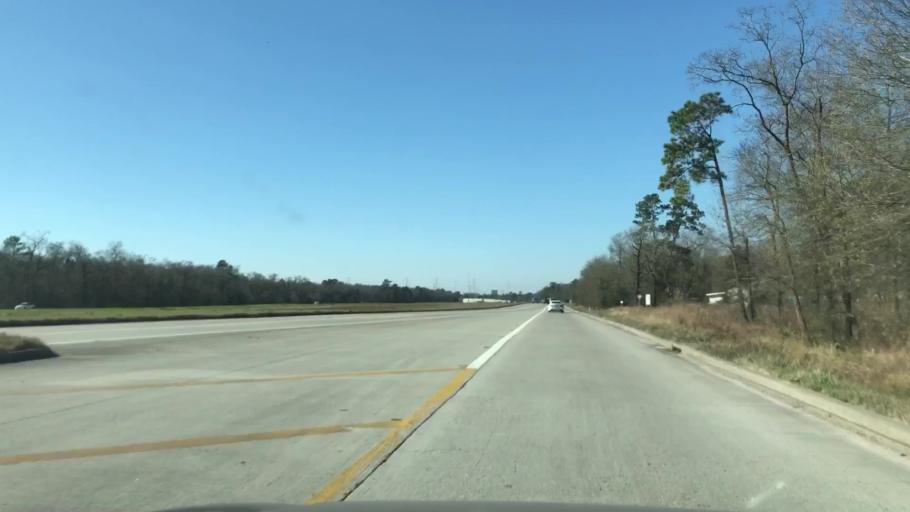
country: US
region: Texas
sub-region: Harris County
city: Cloverleaf
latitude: 29.8271
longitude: -95.1898
